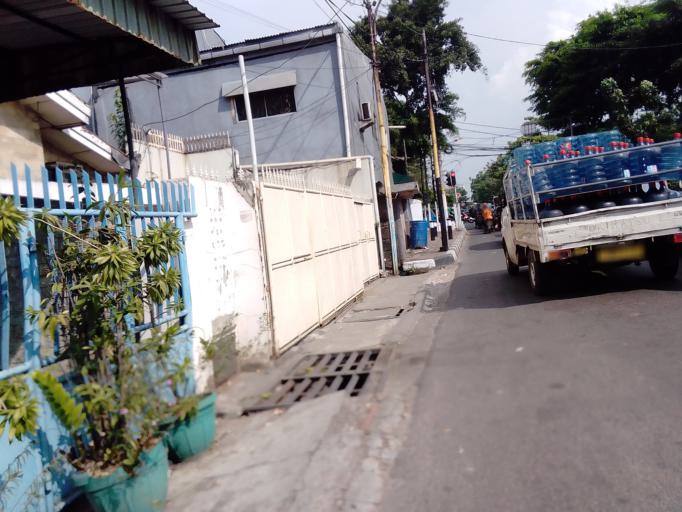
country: ID
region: Jakarta Raya
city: Jakarta
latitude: -6.1604
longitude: 106.8110
